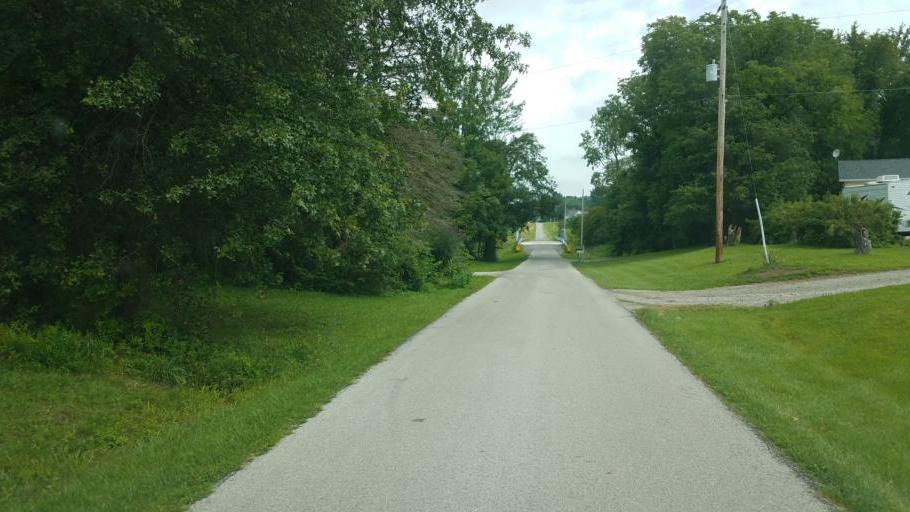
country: US
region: Ohio
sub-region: Morrow County
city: Cardington
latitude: 40.5125
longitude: -82.9401
